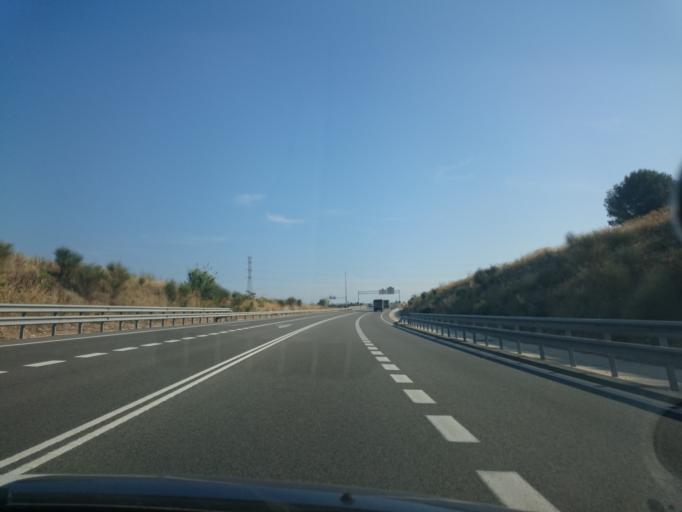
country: ES
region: Catalonia
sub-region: Provincia de Barcelona
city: La Granada
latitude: 41.3576
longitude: 1.7214
